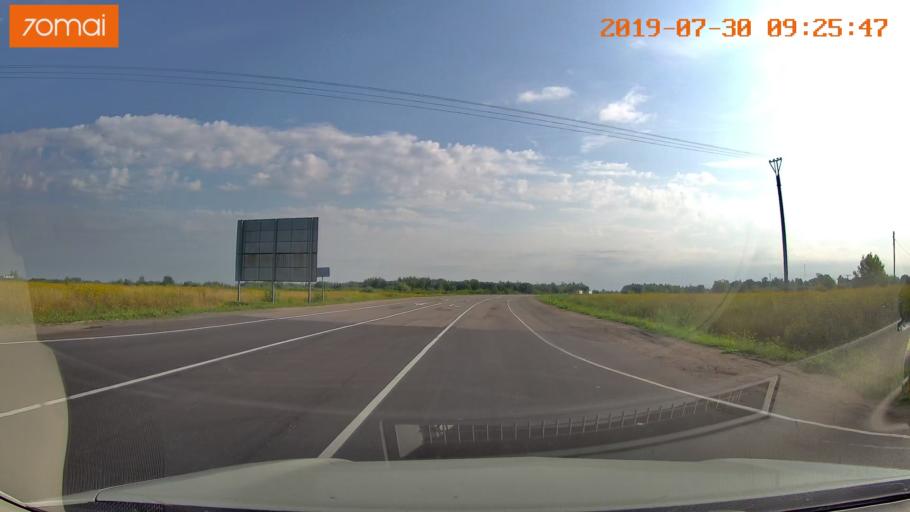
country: LT
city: Kybartai
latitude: 54.6433
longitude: 22.7218
